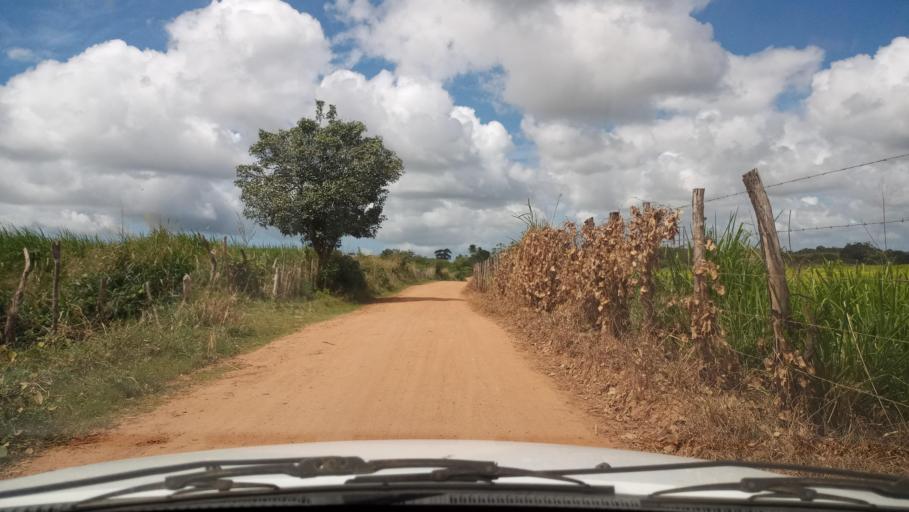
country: BR
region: Rio Grande do Norte
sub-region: Goianinha
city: Goianinha
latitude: -6.2616
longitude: -35.2420
